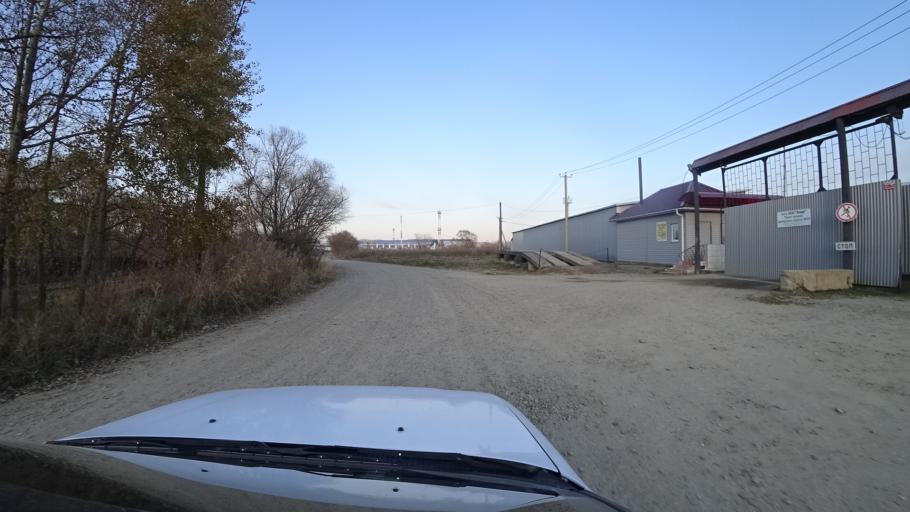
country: RU
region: Primorskiy
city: Dal'nerechensk
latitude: 45.9431
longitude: 133.8254
